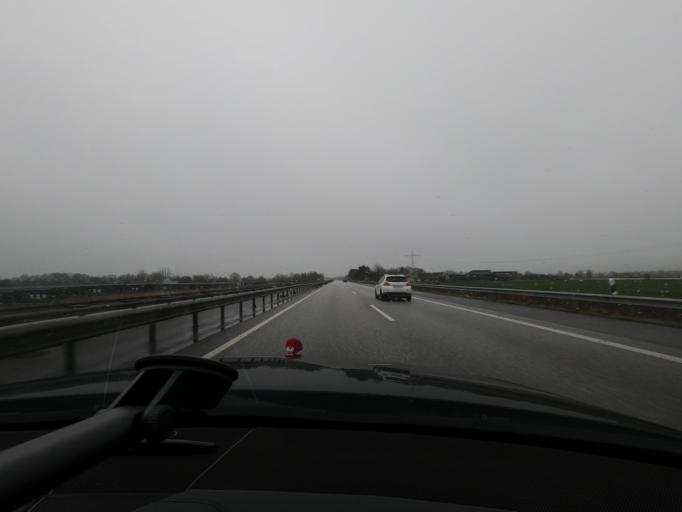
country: DE
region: Schleswig-Holstein
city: Lurschau
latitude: 54.5634
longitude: 9.4685
